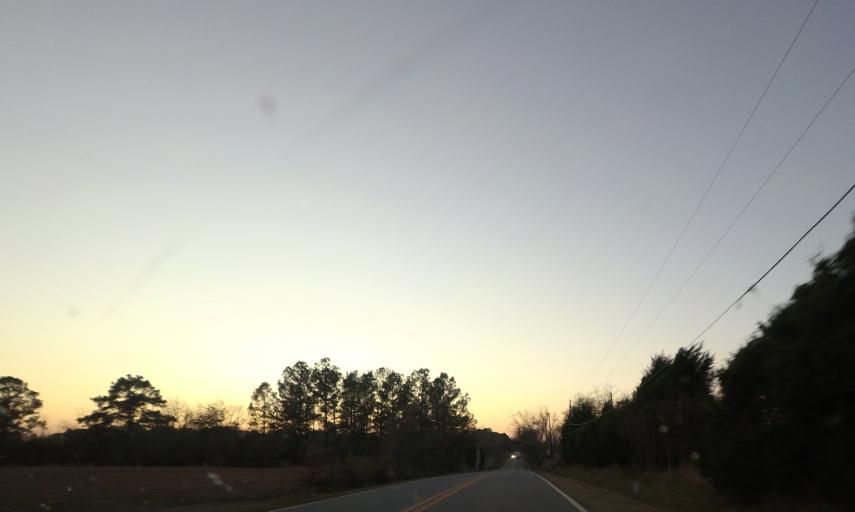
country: US
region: Georgia
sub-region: Houston County
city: Centerville
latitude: 32.7249
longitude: -83.6647
